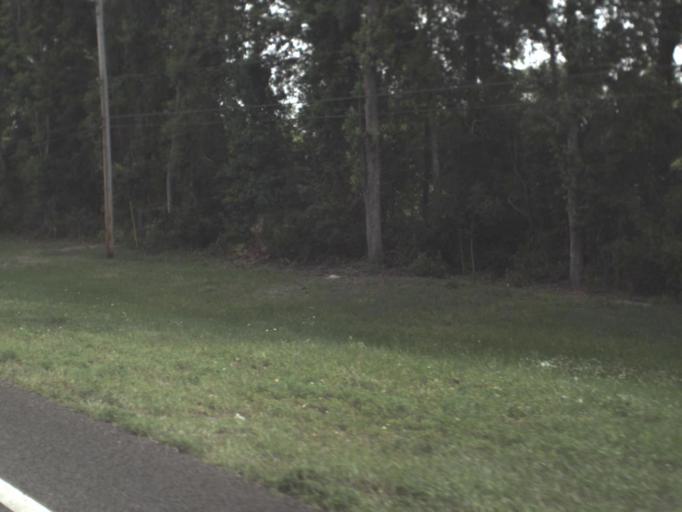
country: US
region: Florida
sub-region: Clay County
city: Green Cove Springs
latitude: 30.0475
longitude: -81.7083
